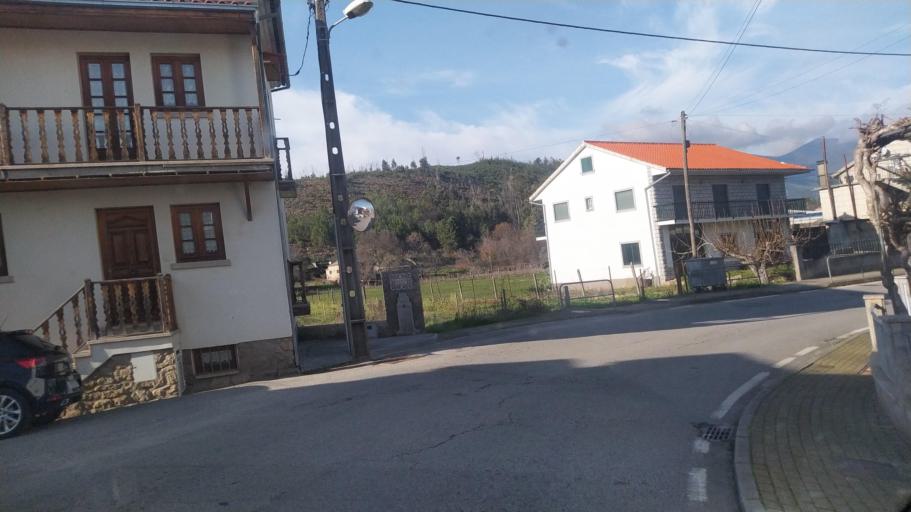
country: PT
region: Castelo Branco
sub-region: Concelho do Fundao
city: Aldeia de Joanes
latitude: 40.2036
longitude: -7.6394
